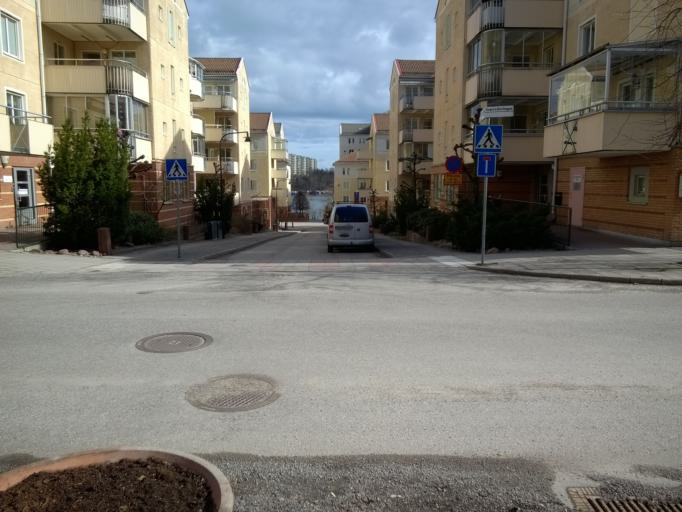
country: SE
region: Stockholm
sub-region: Solna Kommun
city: Solna
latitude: 59.3398
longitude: 17.9892
